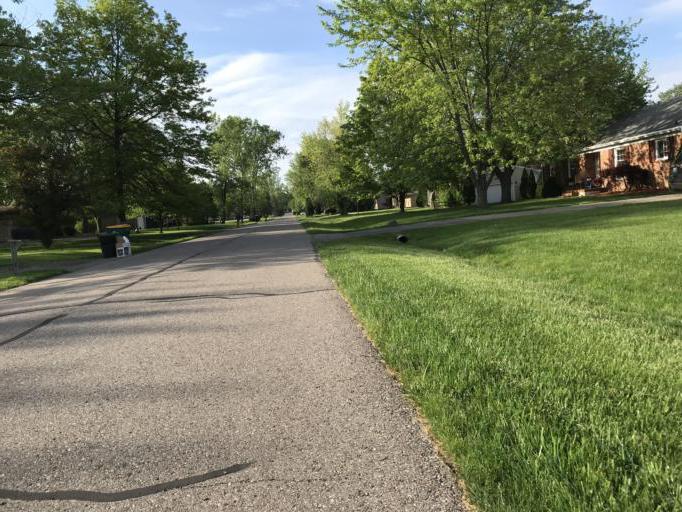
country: US
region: Michigan
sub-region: Oakland County
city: Farmington
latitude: 42.4732
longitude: -83.3445
